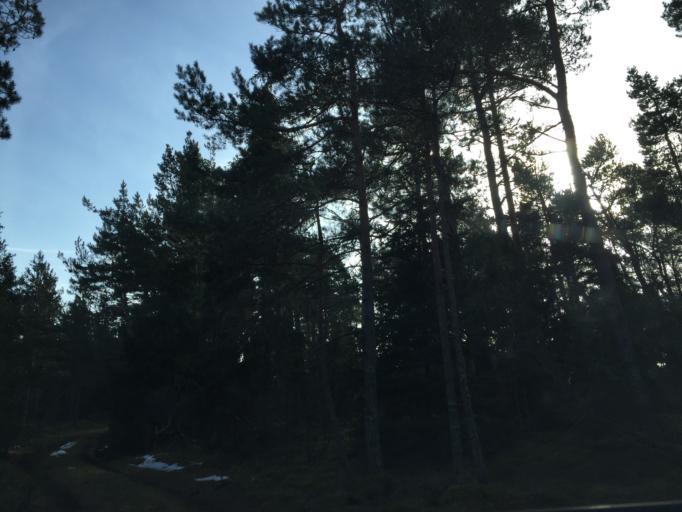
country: EE
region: Saare
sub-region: Kuressaare linn
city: Kuressaare
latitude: 58.3773
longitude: 21.9980
